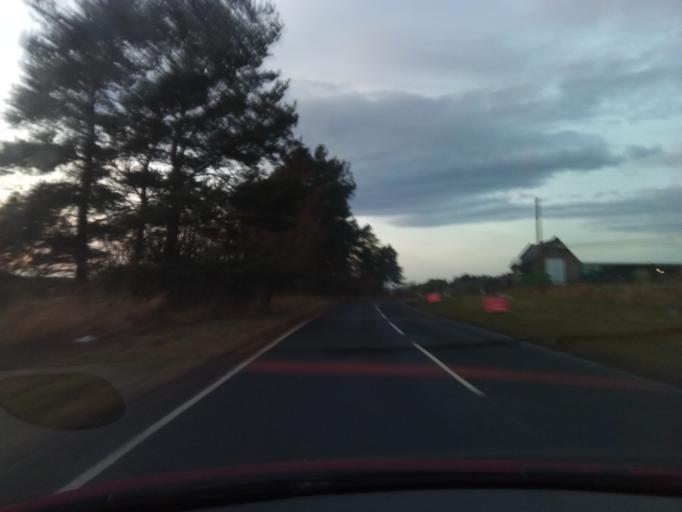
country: GB
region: England
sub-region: Northumberland
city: Otterburn
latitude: 55.2332
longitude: -2.1899
